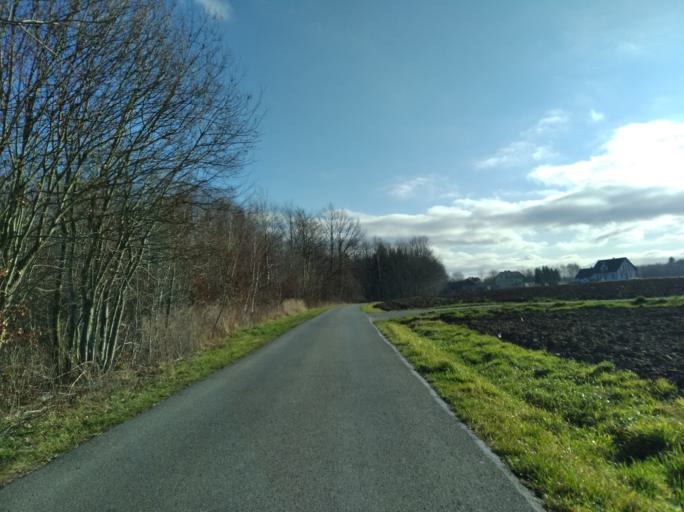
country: PL
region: Subcarpathian Voivodeship
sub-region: Powiat strzyzowski
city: Czudec
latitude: 49.9178
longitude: 21.8412
